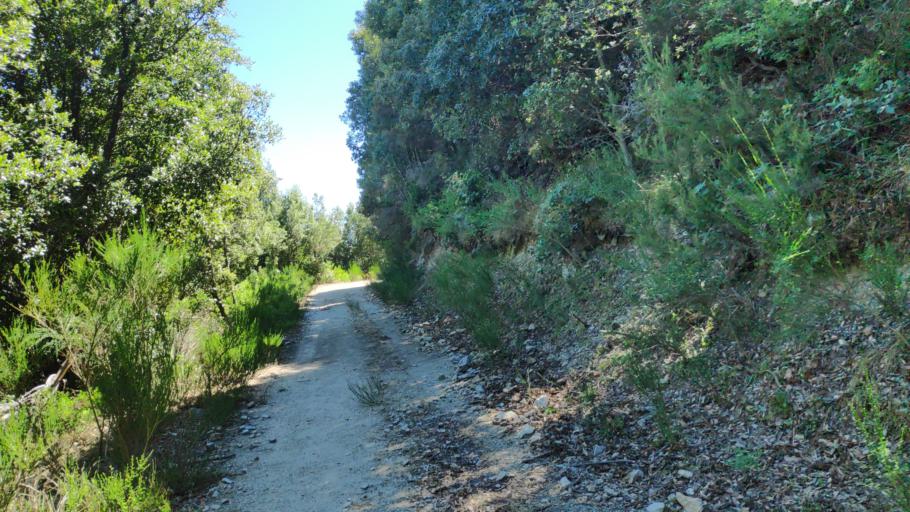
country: IT
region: Calabria
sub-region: Provincia di Vibo-Valentia
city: Nardodipace
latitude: 38.4798
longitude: 16.3857
